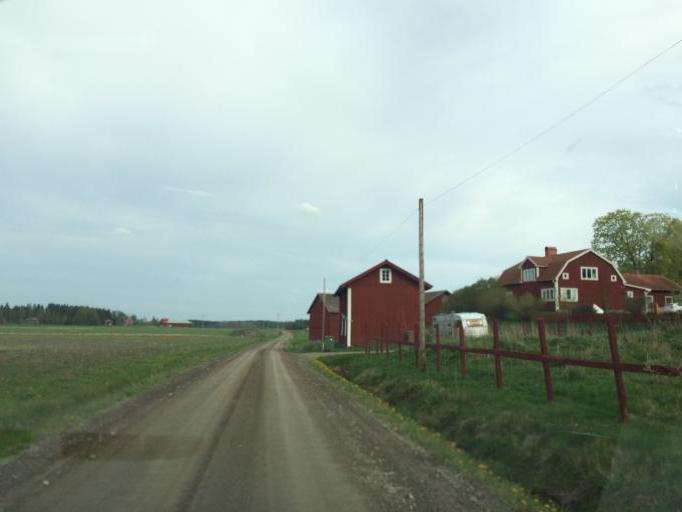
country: SE
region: Vaestmanland
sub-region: Kopings Kommun
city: Koping
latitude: 59.6105
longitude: 16.0608
